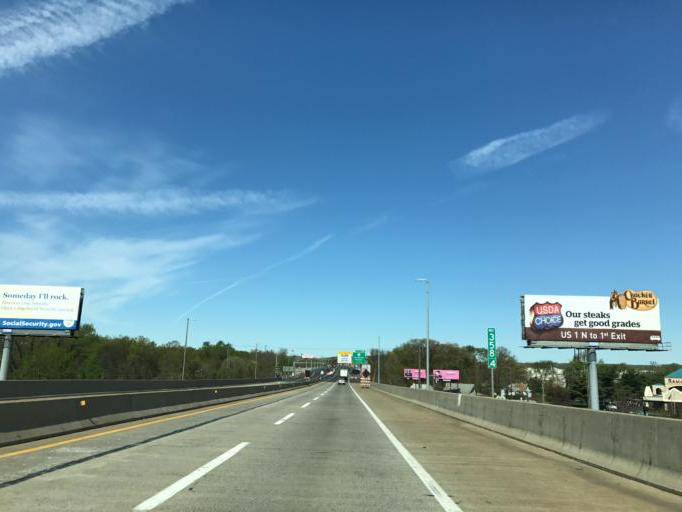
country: US
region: Pennsylvania
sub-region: Bucks County
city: Bristol
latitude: 40.1201
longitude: -74.8413
